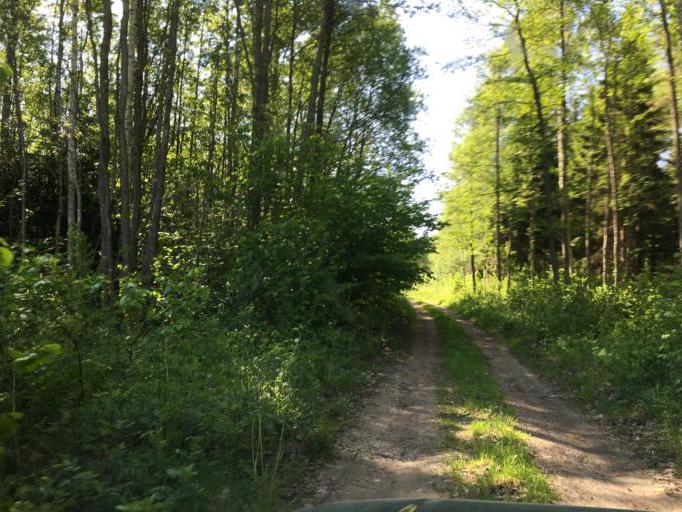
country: LV
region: Ventspils
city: Ventspils
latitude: 57.4777
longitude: 21.7630
